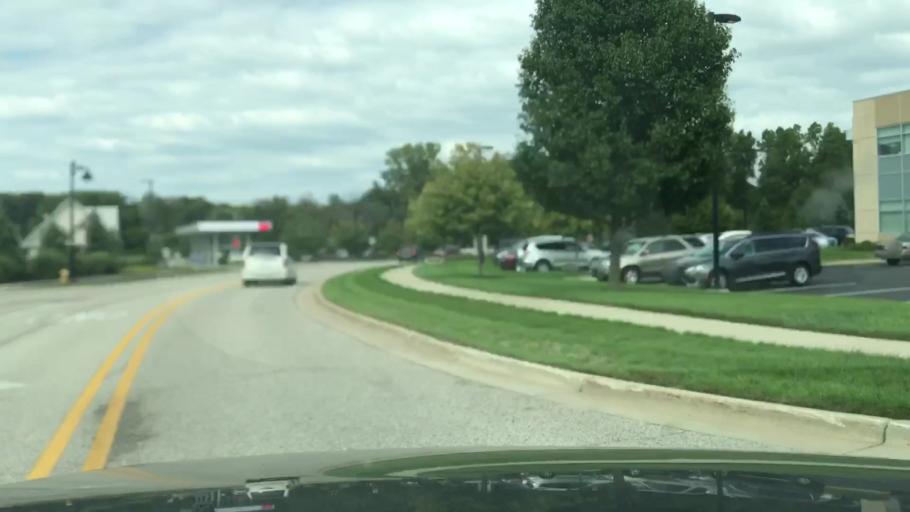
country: US
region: Michigan
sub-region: Kent County
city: Byron Center
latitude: 42.8599
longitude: -85.7194
